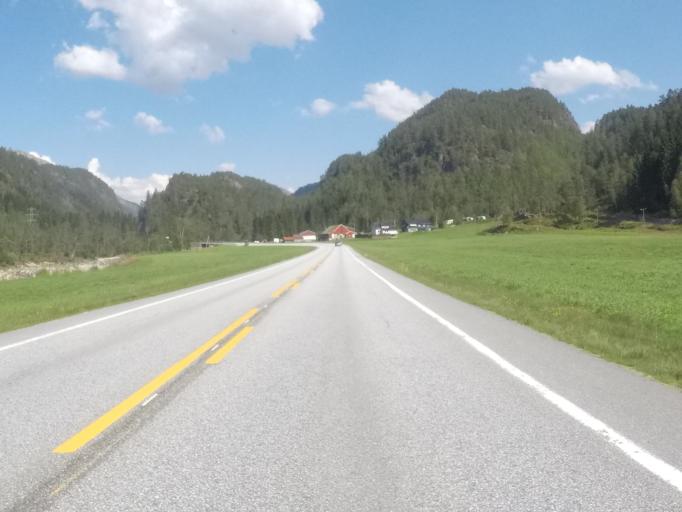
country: NO
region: Hordaland
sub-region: Modalen
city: Mo
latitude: 60.7509
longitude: 5.6277
